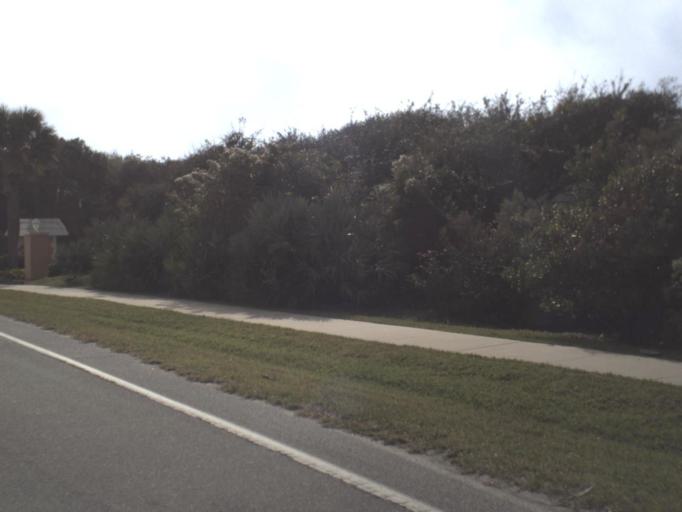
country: US
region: Florida
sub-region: Volusia County
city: Edgewater
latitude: 29.0038
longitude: -80.8761
